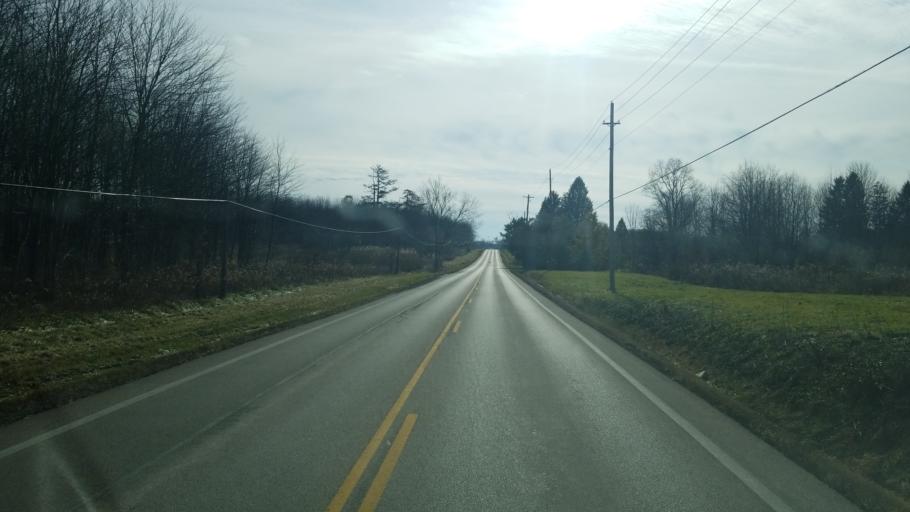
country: US
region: Ohio
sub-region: Ashtabula County
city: Geneva
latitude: 41.7222
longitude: -80.9525
